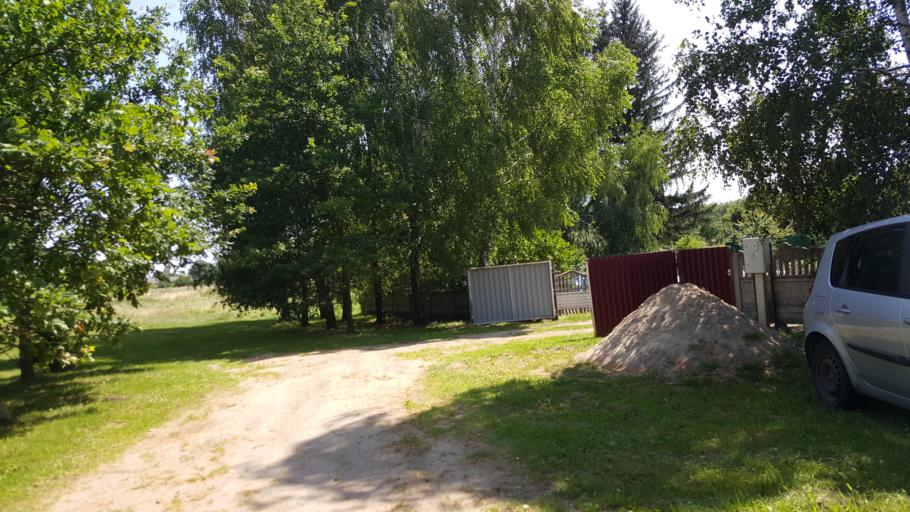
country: BY
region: Brest
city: Vysokaye
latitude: 52.3672
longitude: 23.3930
